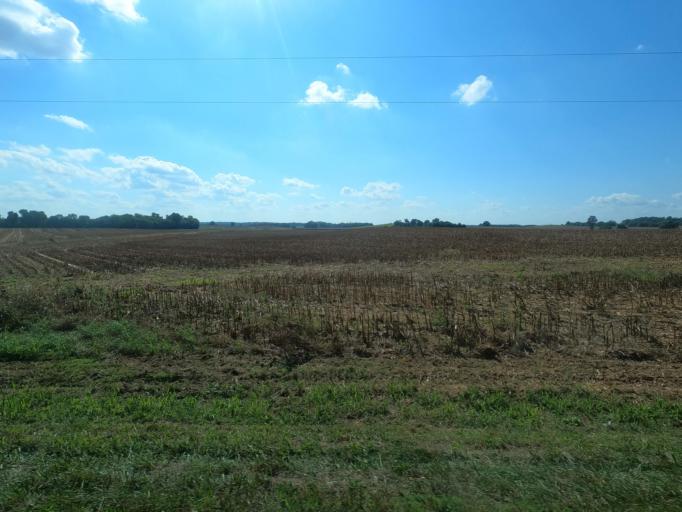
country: US
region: Illinois
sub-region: Massac County
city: Metropolis
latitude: 37.2619
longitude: -88.7596
